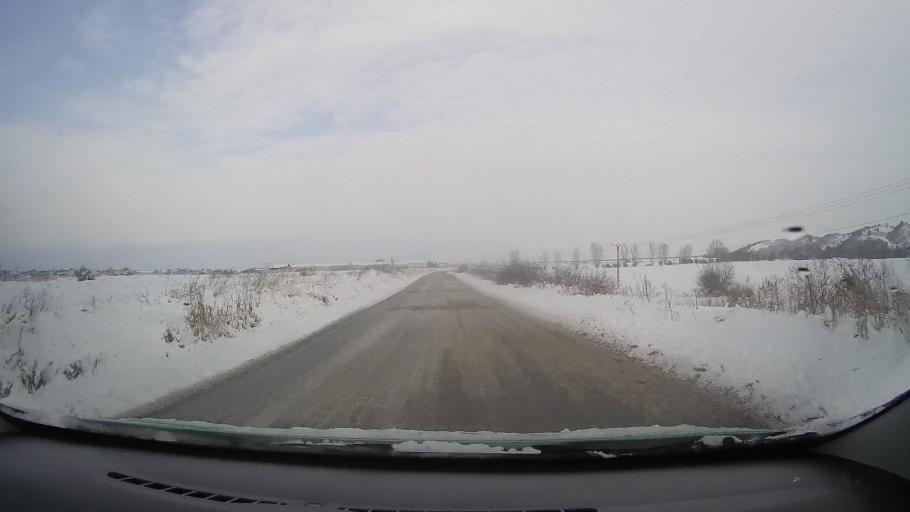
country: RO
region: Alba
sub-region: Comuna Pianu
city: Pianu de Jos
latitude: 45.9552
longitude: 23.4776
